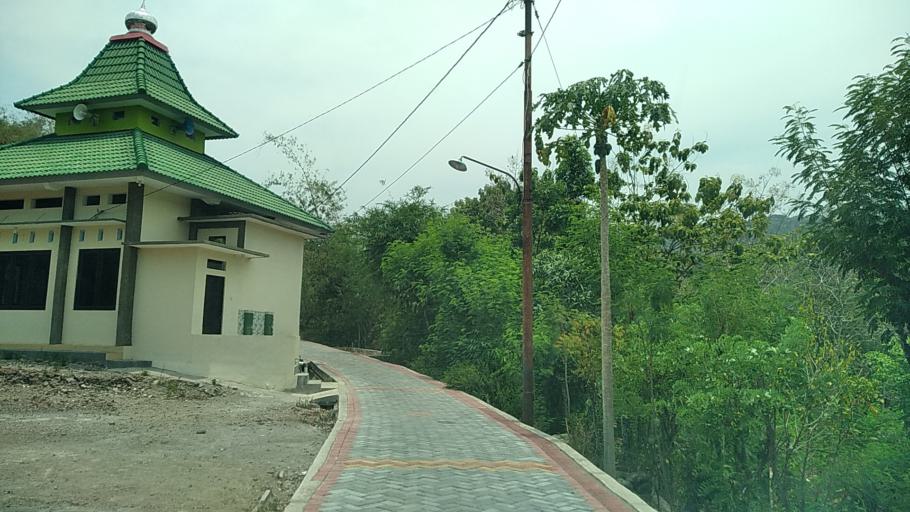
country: ID
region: Central Java
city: Semarang
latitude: -7.0436
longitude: 110.4054
